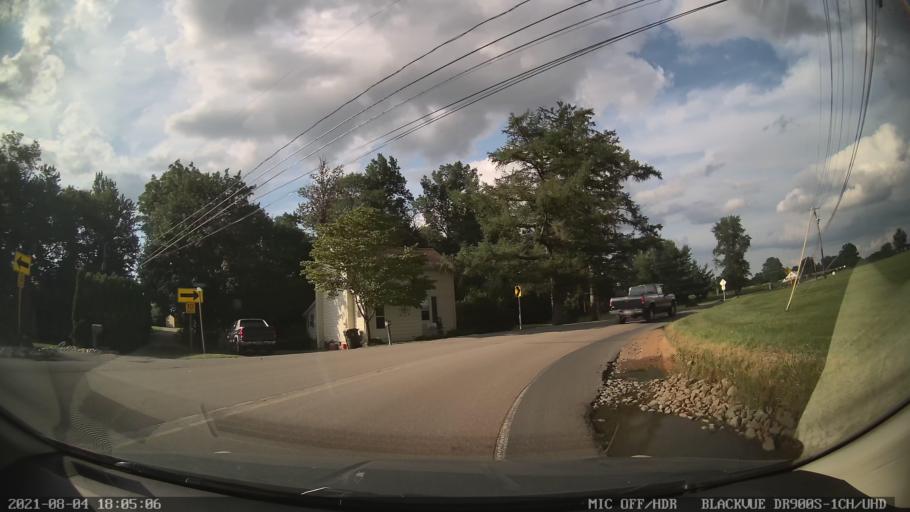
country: US
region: Pennsylvania
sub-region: Lehigh County
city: Trexlertown
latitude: 40.5600
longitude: -75.5989
